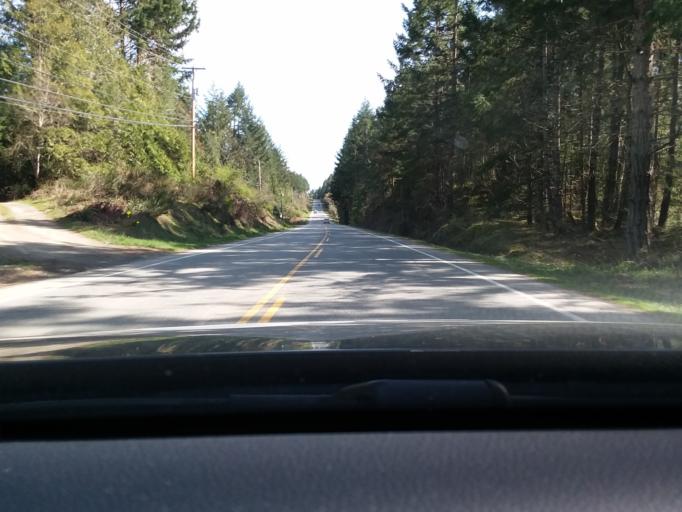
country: CA
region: British Columbia
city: North Cowichan
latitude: 48.8632
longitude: -123.4933
